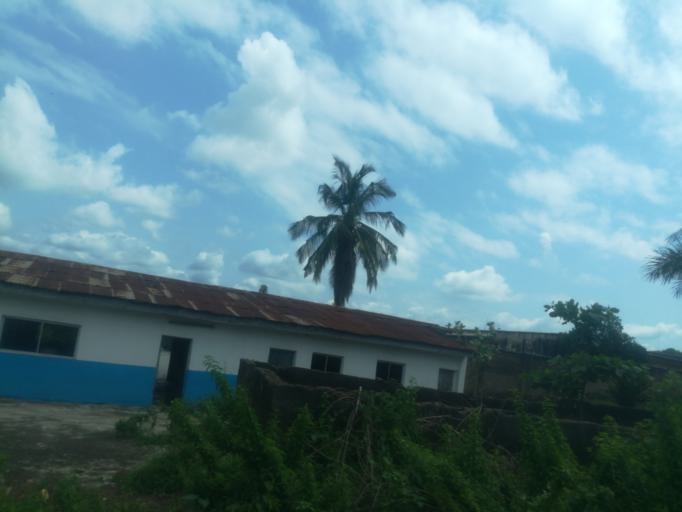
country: NG
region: Oyo
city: Egbeda
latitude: 7.4201
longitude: 3.9993
